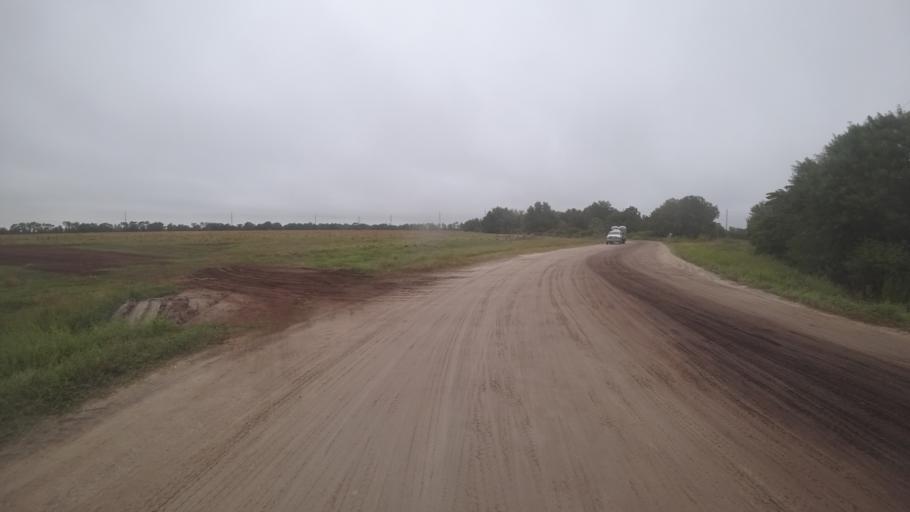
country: US
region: Florida
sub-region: Sarasota County
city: The Meadows
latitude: 27.4715
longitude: -82.3448
